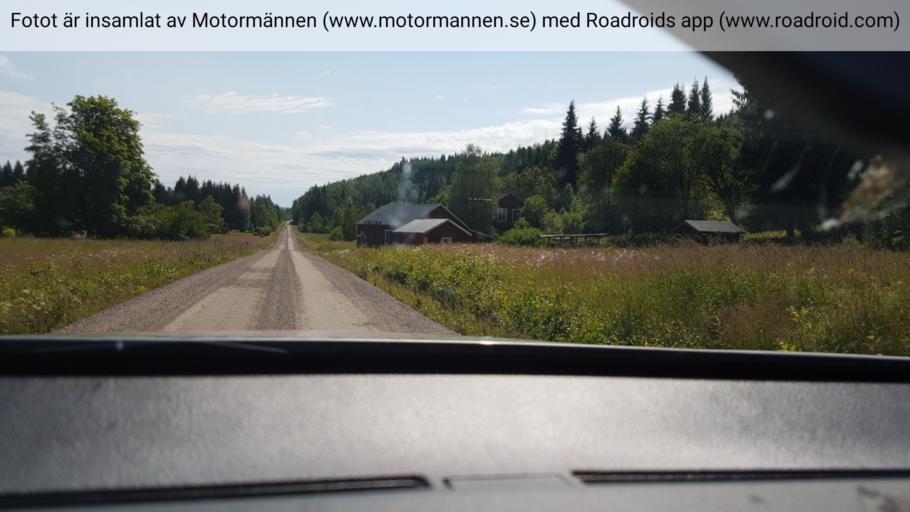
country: SE
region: Vaermland
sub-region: Torsby Kommun
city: Torsby
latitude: 60.4696
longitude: 13.1837
